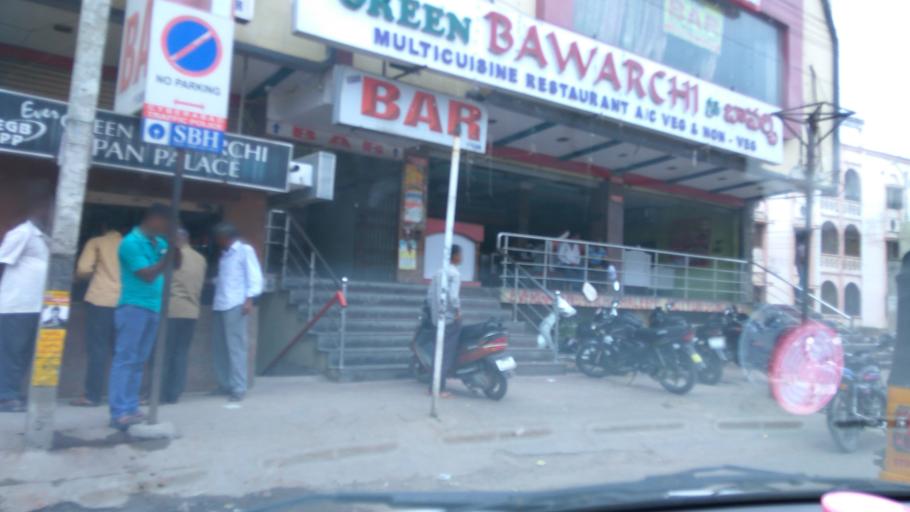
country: IN
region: Telangana
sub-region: Hyderabad
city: Malkajgiri
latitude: 17.4444
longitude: 78.5339
